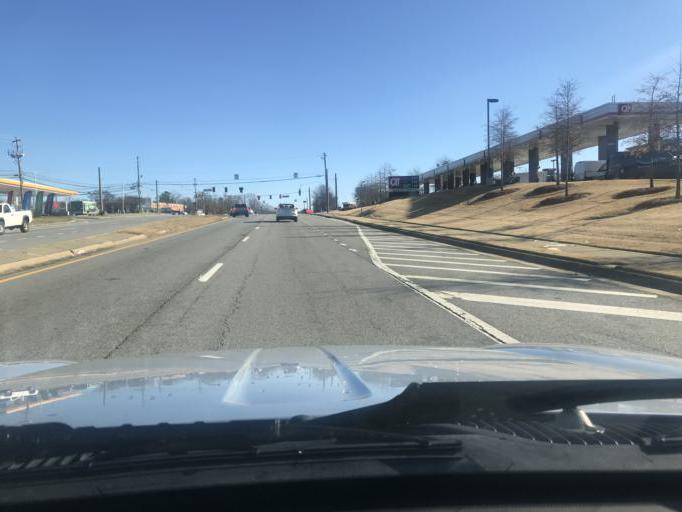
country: US
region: Georgia
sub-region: Gwinnett County
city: Lawrenceville
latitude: 33.9679
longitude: -84.0371
